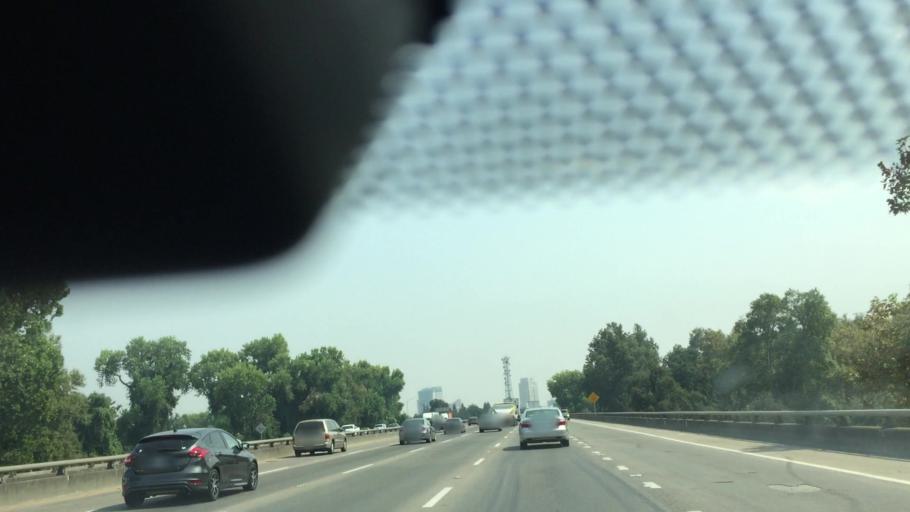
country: US
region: California
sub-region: Sacramento County
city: Sacramento
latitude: 38.6035
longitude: -121.5068
